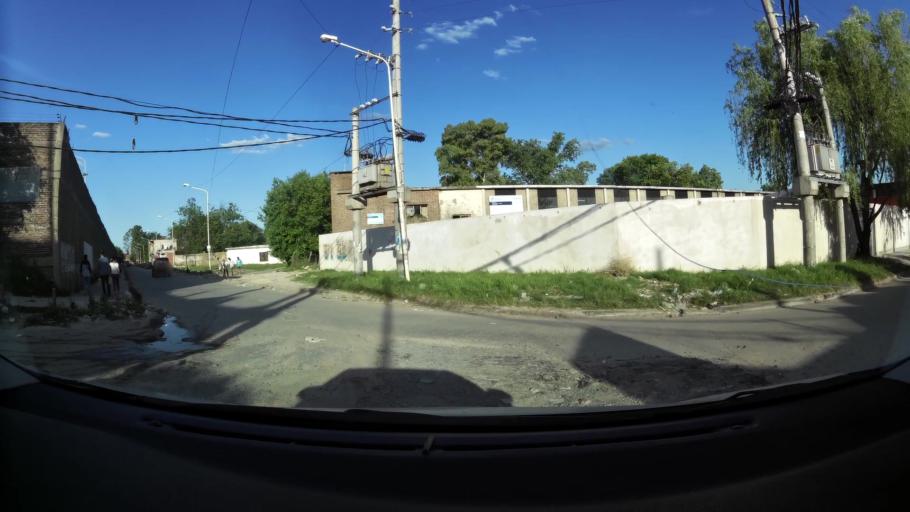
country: AR
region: Buenos Aires F.D.
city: Villa Lugano
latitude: -34.7072
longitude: -58.4817
